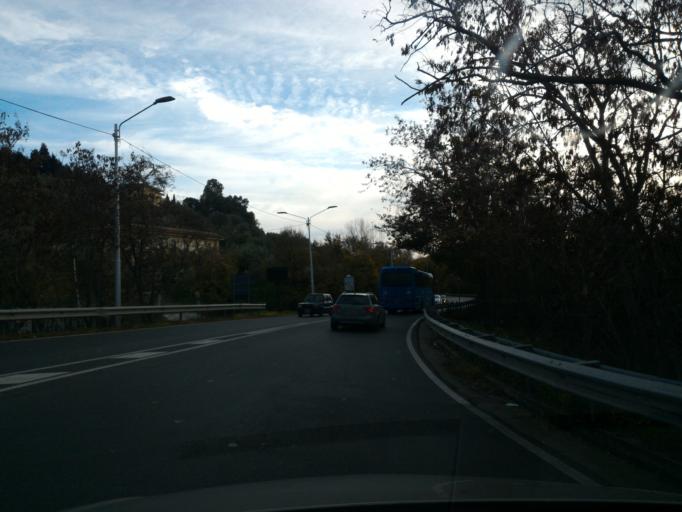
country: IT
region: Calabria
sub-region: Provincia di Catanzaro
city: Catanzaro
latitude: 38.8797
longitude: 16.6045
